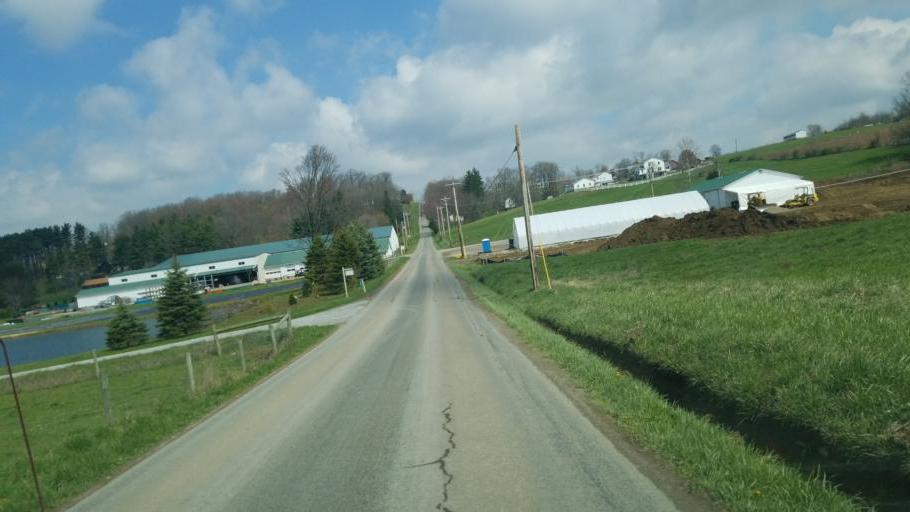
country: US
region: Ohio
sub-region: Wayne County
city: Apple Creek
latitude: 40.6809
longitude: -81.8422
